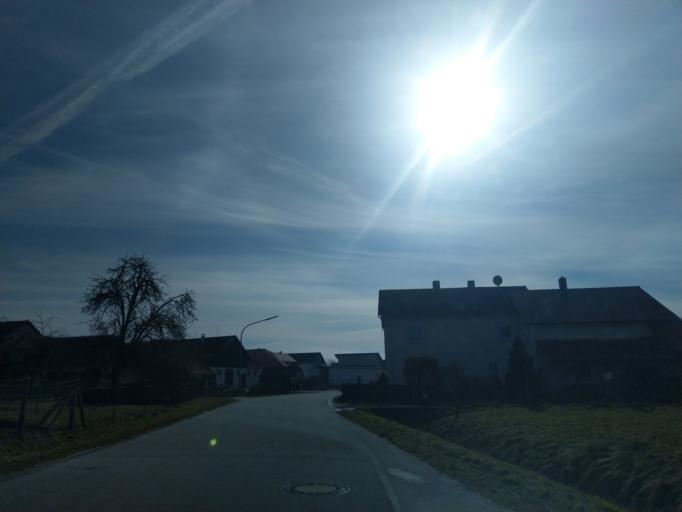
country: DE
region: Bavaria
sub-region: Lower Bavaria
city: Buchhofen
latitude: 48.6705
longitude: 12.9638
